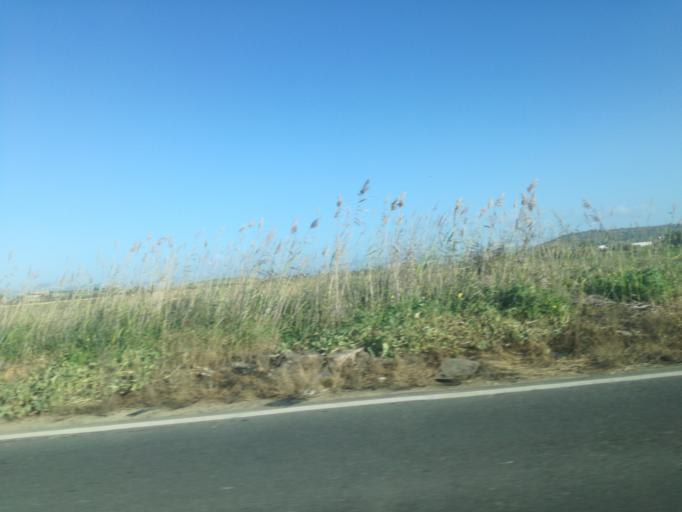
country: IT
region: Sicily
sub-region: Provincia di Caltanissetta
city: Gela
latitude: 37.0548
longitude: 14.3004
